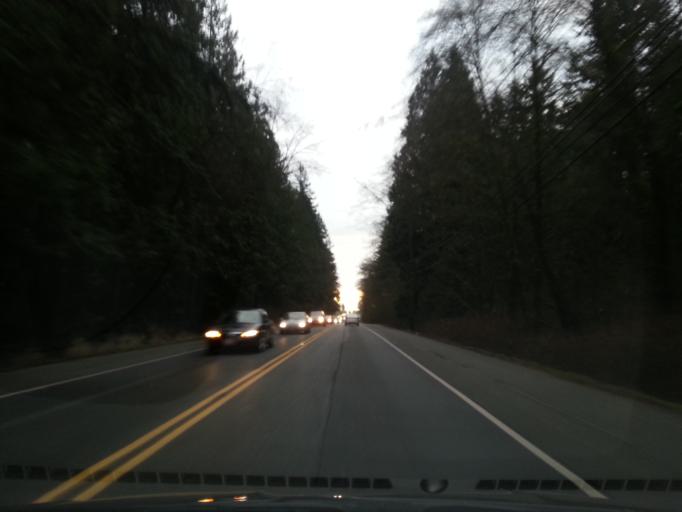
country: CA
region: British Columbia
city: Surrey
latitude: 49.1722
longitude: -122.8174
